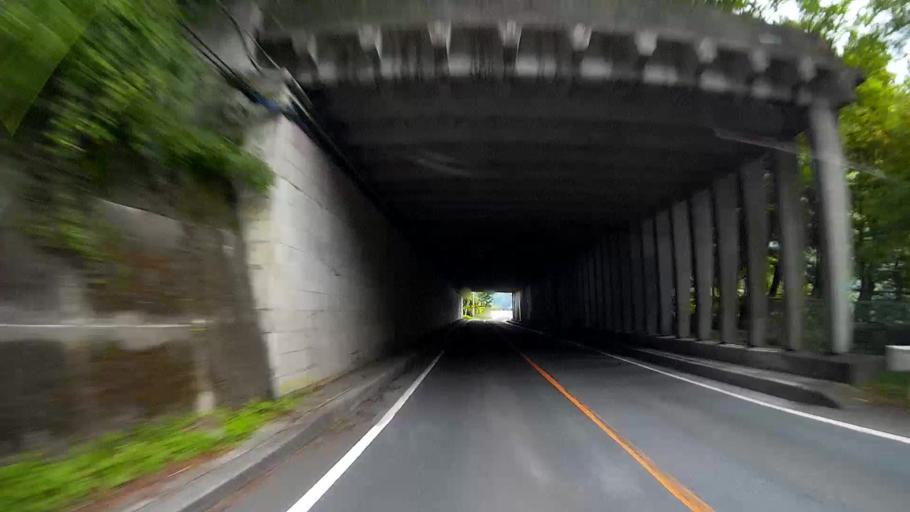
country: JP
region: Yamanashi
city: Enzan
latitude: 35.9154
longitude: 138.8307
